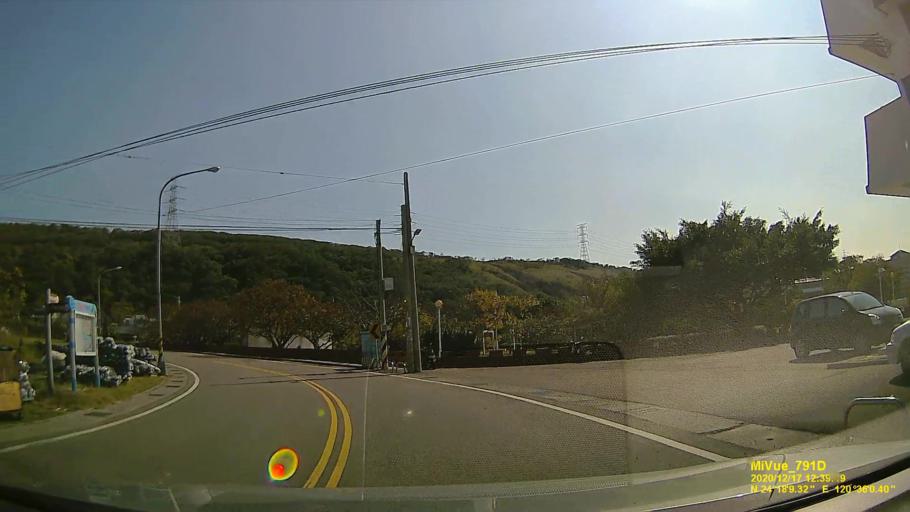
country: TW
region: Taiwan
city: Fengyuan
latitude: 24.3028
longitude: 120.6001
